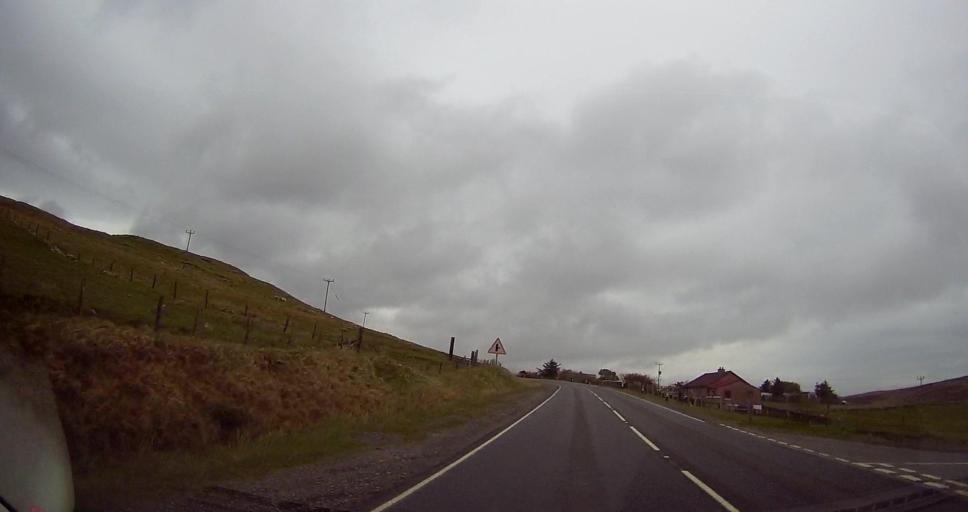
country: GB
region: Scotland
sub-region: Shetland Islands
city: Lerwick
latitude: 60.2390
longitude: -1.2294
